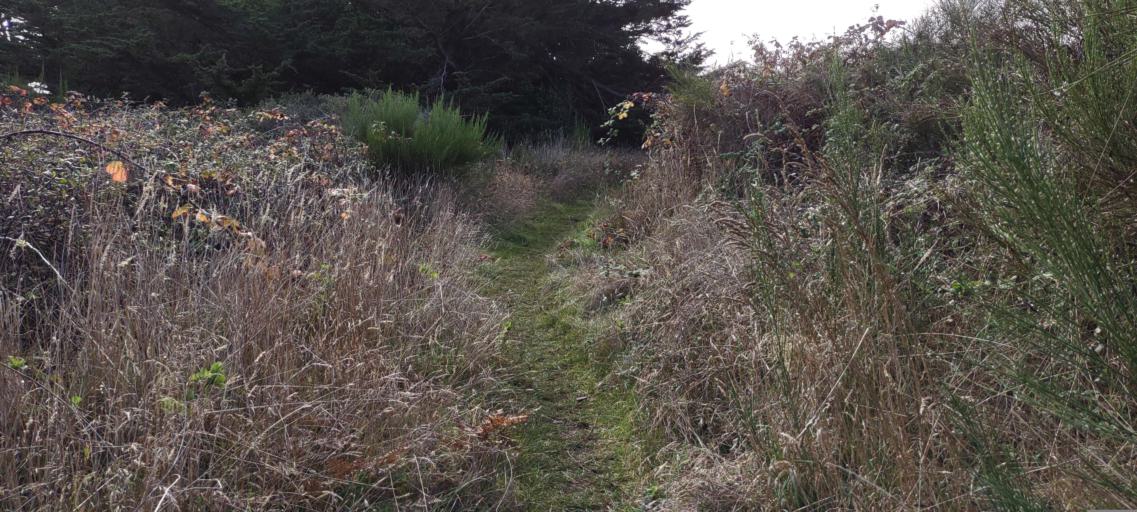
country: US
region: California
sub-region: Mendocino County
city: Fort Bragg
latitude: 39.3108
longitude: -123.8032
